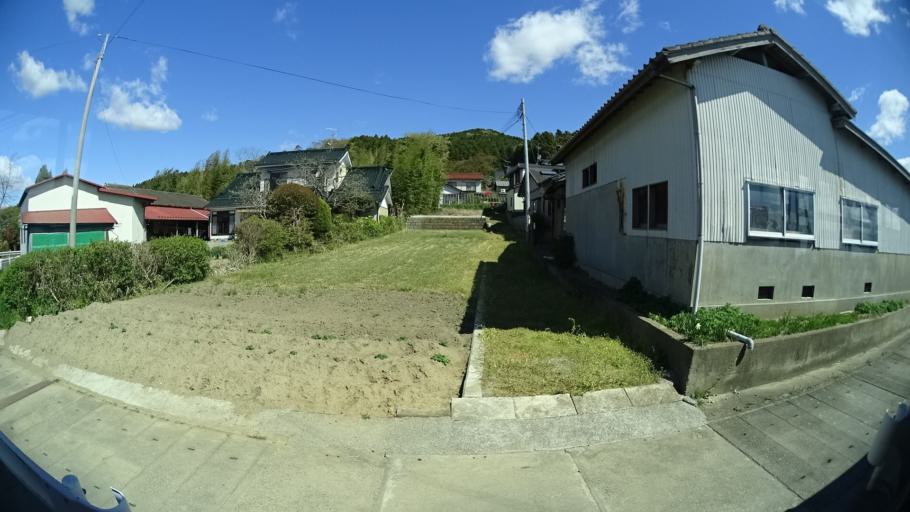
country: JP
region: Miyagi
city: Wakuya
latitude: 38.5213
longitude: 141.2078
